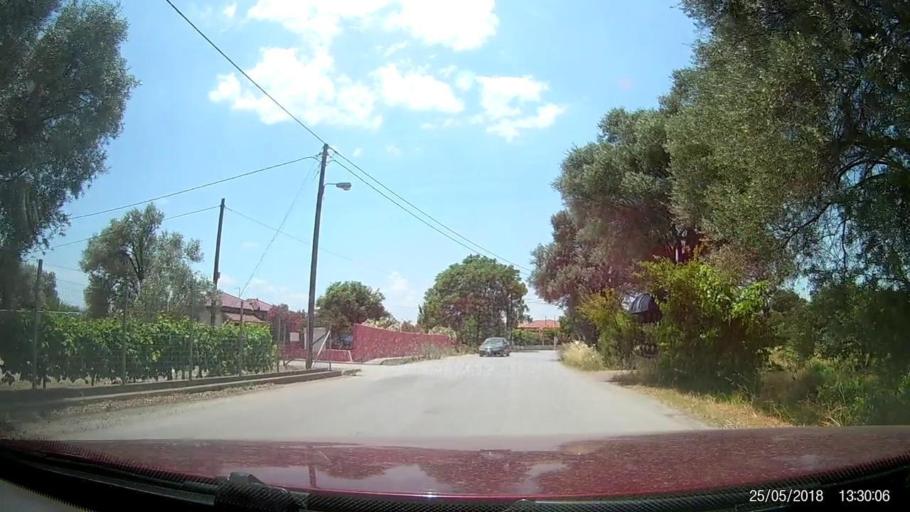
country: GR
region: Central Greece
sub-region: Nomos Evvoias
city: Mytikas
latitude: 38.4423
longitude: 23.6588
